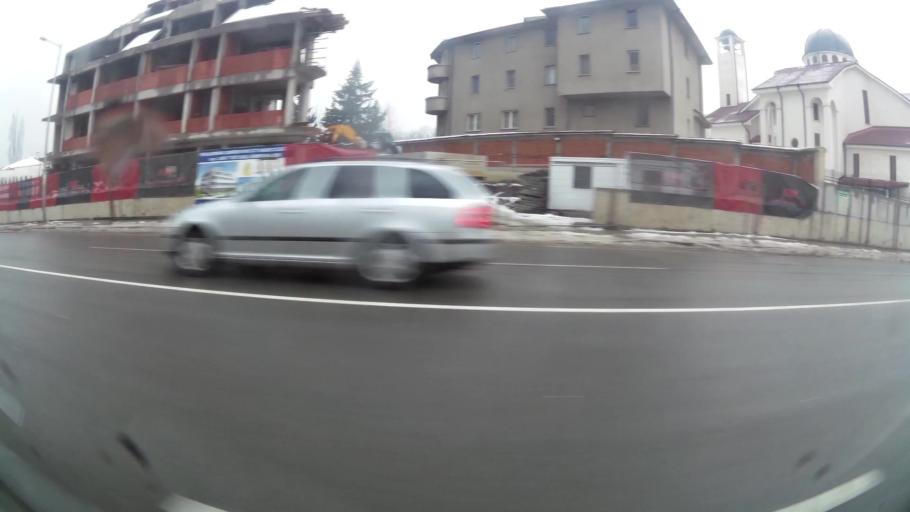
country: BG
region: Sofia-Capital
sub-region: Stolichna Obshtina
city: Sofia
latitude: 42.6755
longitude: 23.2529
